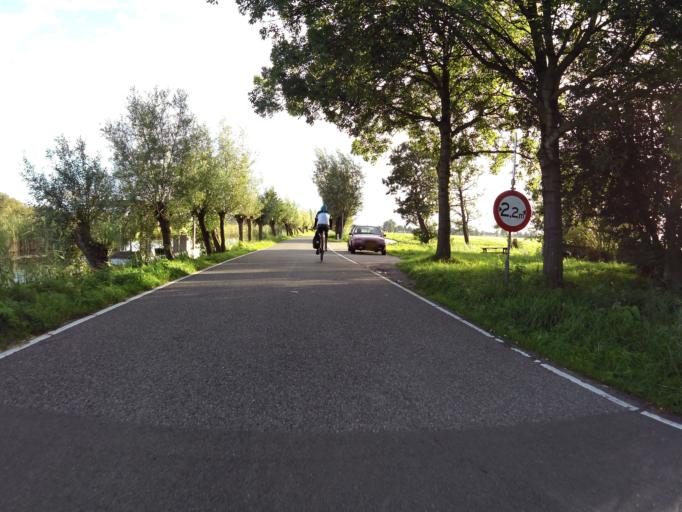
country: NL
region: South Holland
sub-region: Gemeente Nieuwkoop
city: Nieuwkoop
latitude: 52.1280
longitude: 4.7583
